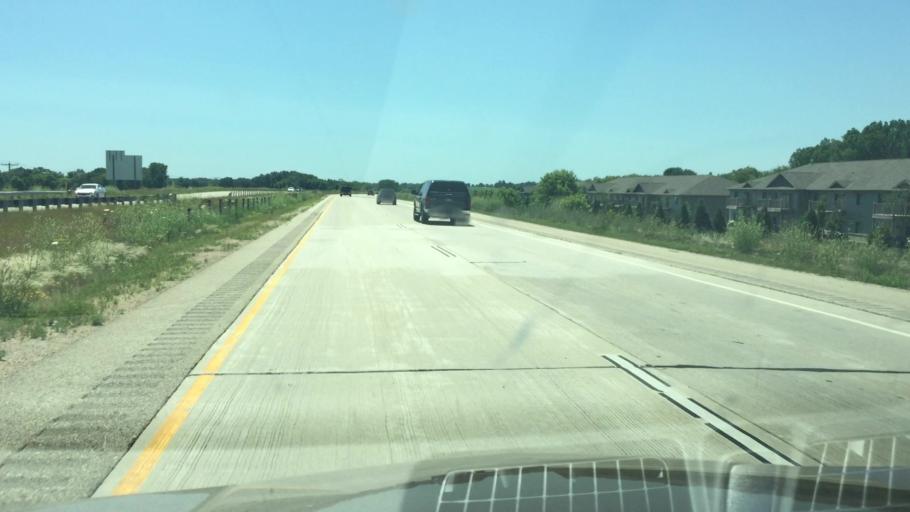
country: US
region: Wisconsin
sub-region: Dodge County
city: Beaver Dam
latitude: 43.4413
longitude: -88.8253
